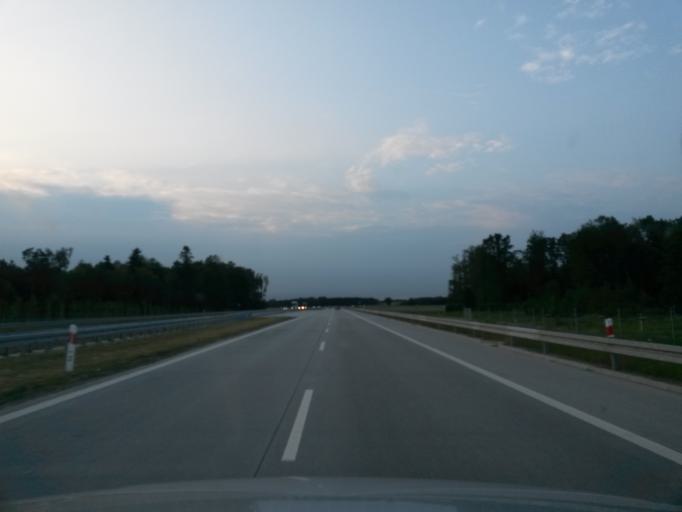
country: PL
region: Lodz Voivodeship
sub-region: Powiat sieradzki
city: Zloczew
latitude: 51.4383
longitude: 18.6460
